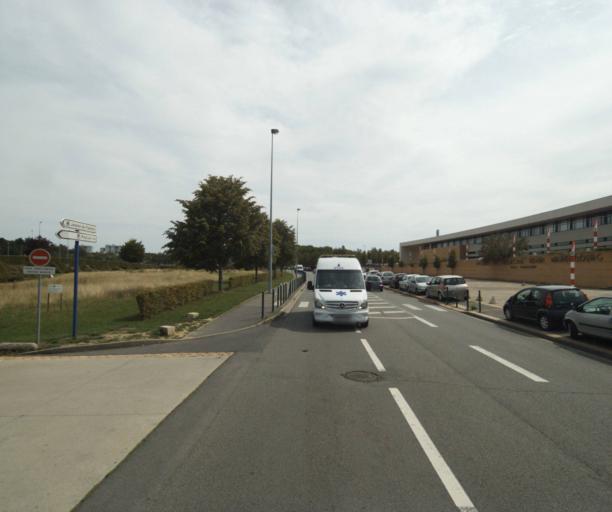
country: FR
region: Nord-Pas-de-Calais
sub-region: Departement du Nord
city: Loos
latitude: 50.6045
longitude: 3.0318
